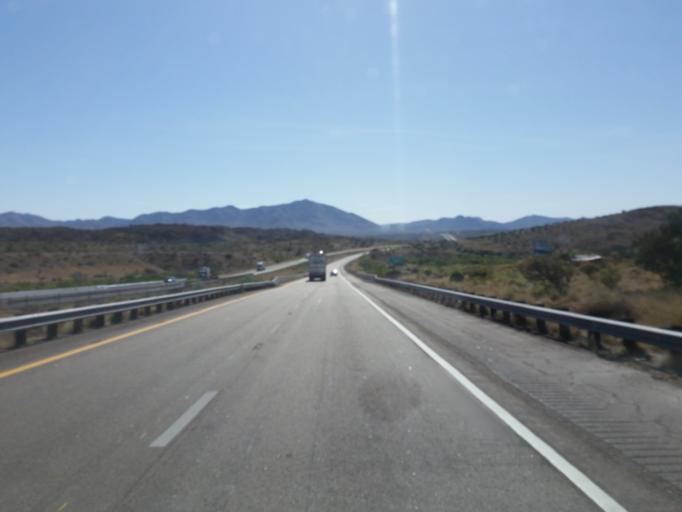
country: US
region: Arizona
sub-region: Mohave County
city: New Kingman-Butler
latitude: 35.1615
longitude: -113.6709
